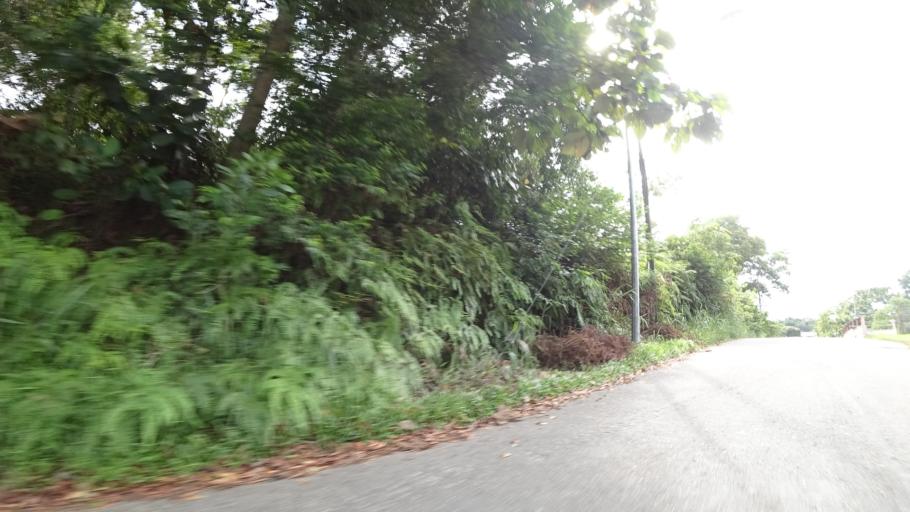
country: BN
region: Brunei and Muara
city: Bandar Seri Begawan
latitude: 4.8687
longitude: 114.9453
